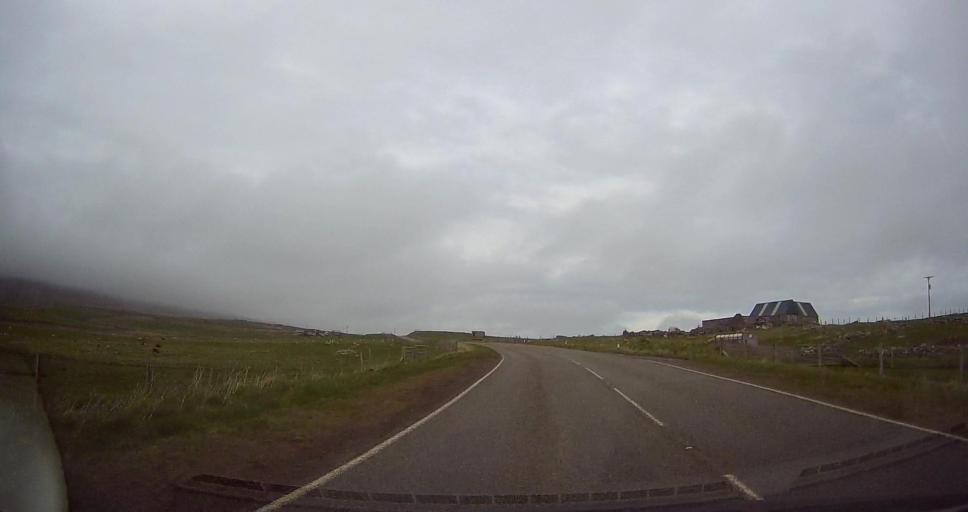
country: GB
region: Scotland
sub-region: Shetland Islands
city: Sandwick
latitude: 59.9301
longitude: -1.2962
